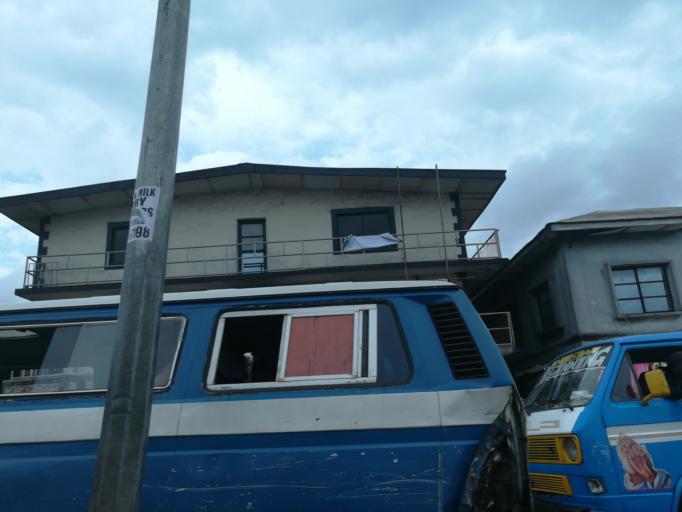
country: NG
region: Rivers
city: Port Harcourt
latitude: 4.7587
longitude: 7.0228
